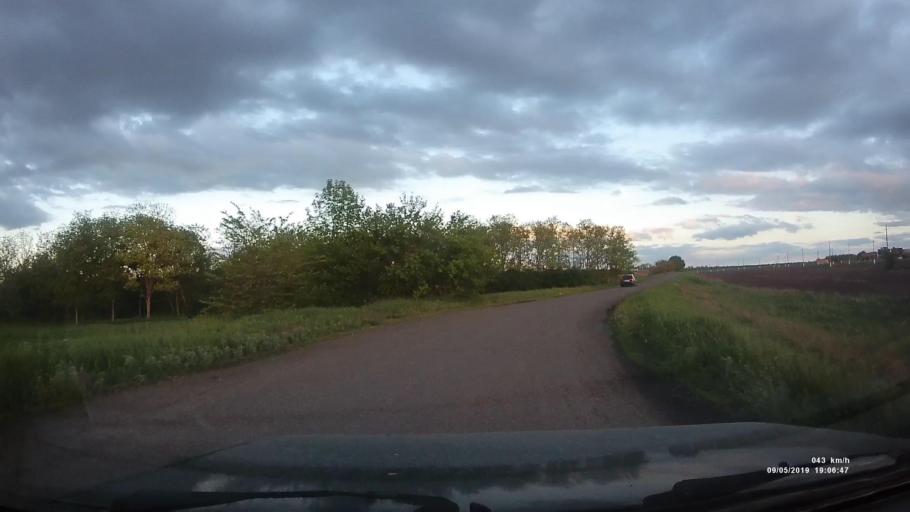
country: RU
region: Krasnodarskiy
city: Kanelovskaya
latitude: 46.7383
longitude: 39.1947
